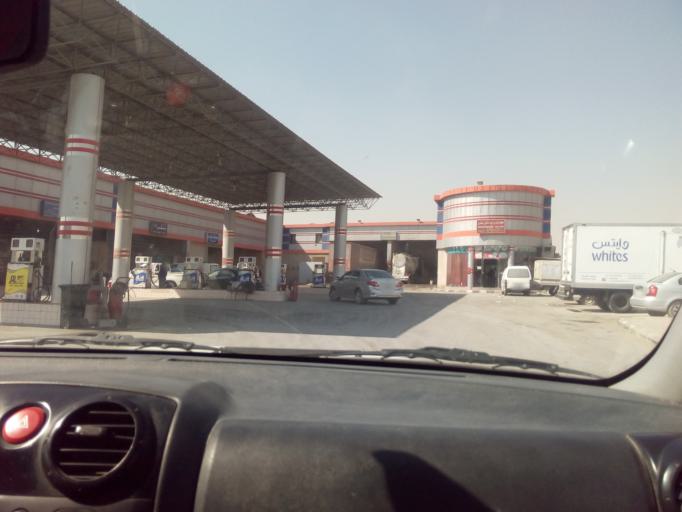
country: SA
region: Ar Riyad
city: Riyadh
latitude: 24.6650
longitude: 46.8422
